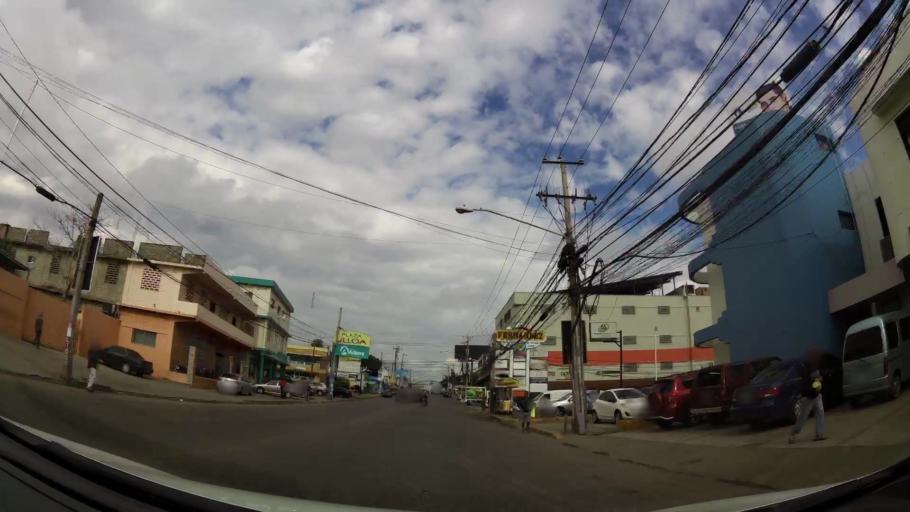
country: DO
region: Santiago
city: Santiago de los Caballeros
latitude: 19.4299
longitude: -70.6896
